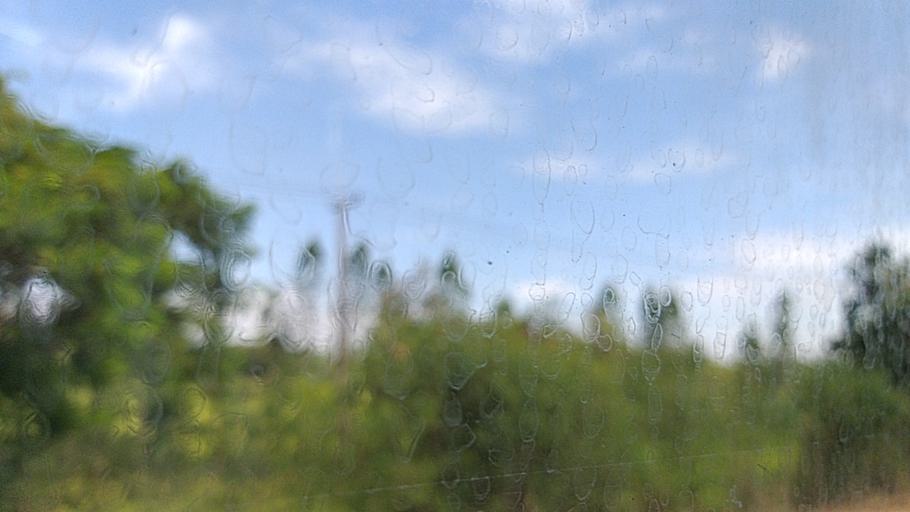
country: TH
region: Khon Kaen
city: Khon Kaen
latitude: 16.4083
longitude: 102.8926
